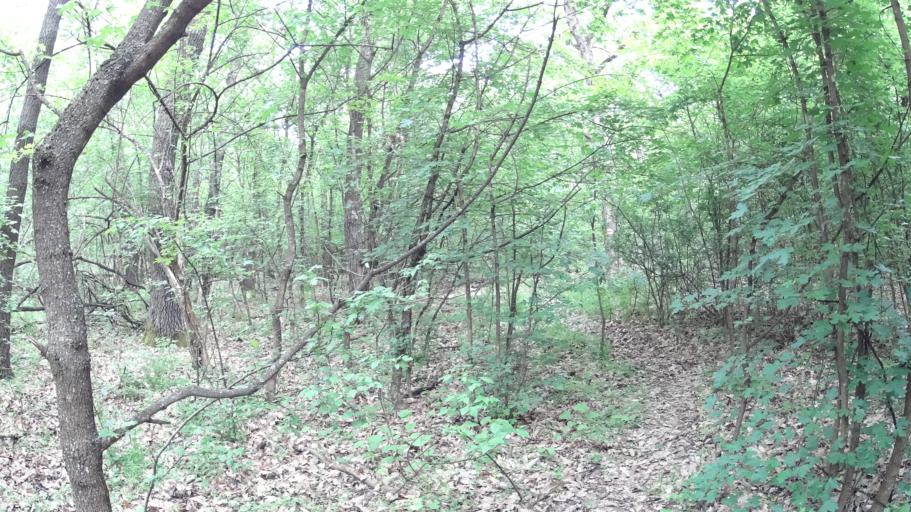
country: HU
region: Pest
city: Acsa
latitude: 47.8235
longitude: 19.3048
